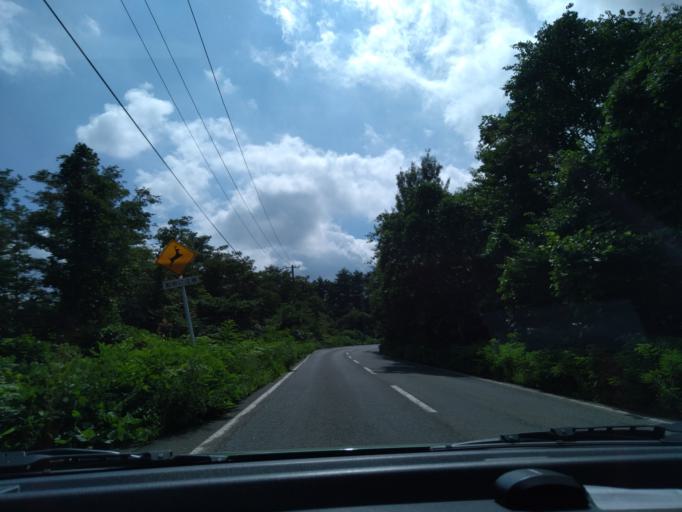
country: JP
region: Iwate
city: Morioka-shi
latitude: 39.6333
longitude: 141.0861
